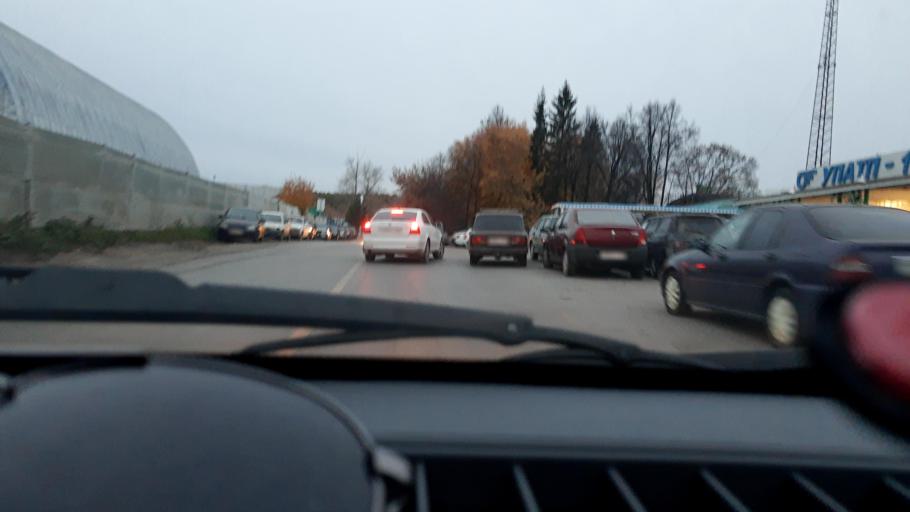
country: RU
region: Bashkortostan
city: Ufa
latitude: 54.8073
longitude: 56.0677
